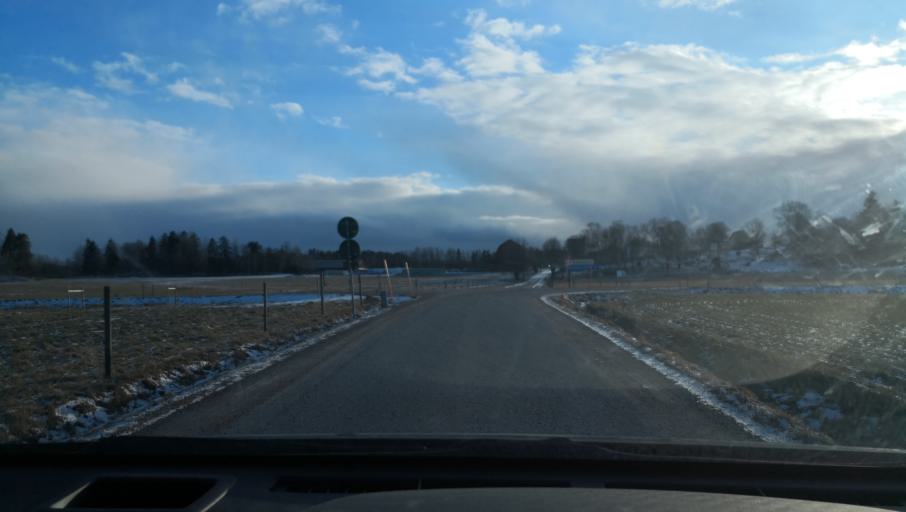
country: SE
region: Uppsala
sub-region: Enkopings Kommun
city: Irsta
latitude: 59.6565
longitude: 16.8035
